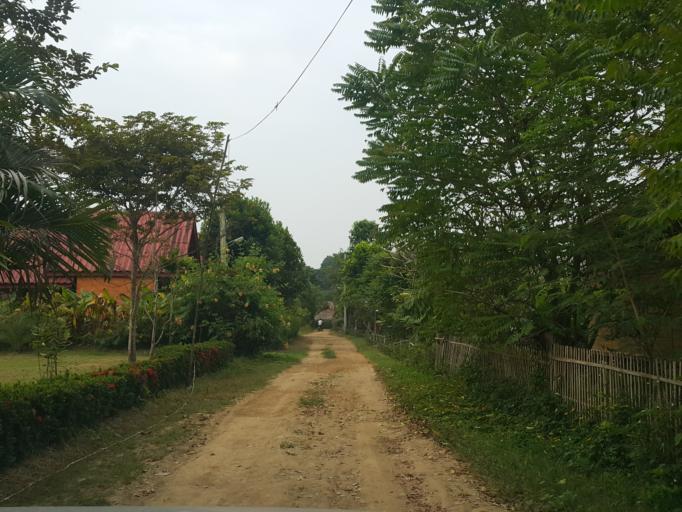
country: TH
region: Chiang Mai
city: Pai
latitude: 19.3617
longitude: 98.4462
